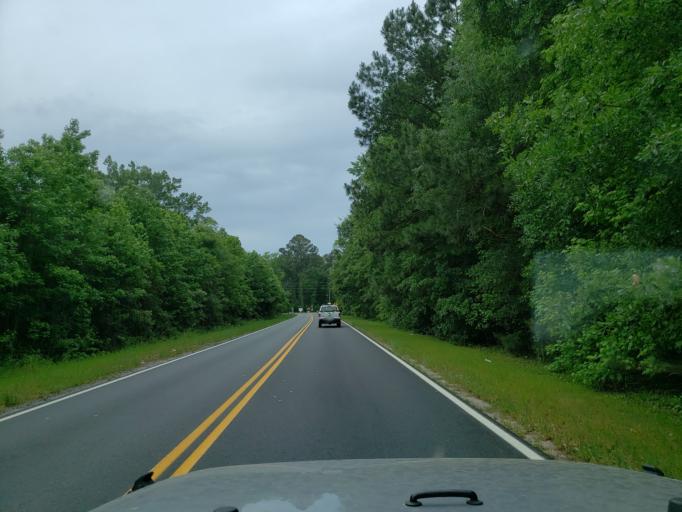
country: US
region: Georgia
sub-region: Chatham County
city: Port Wentworth
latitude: 32.1818
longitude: -81.1949
